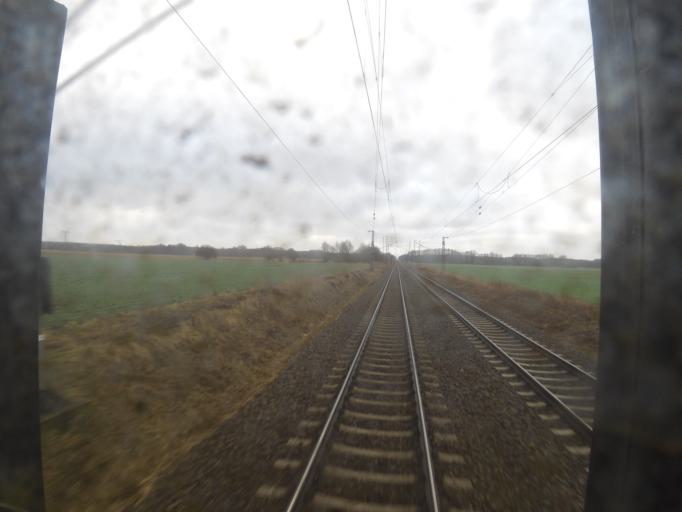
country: DE
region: Brandenburg
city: Zossen
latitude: 52.2013
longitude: 13.4445
